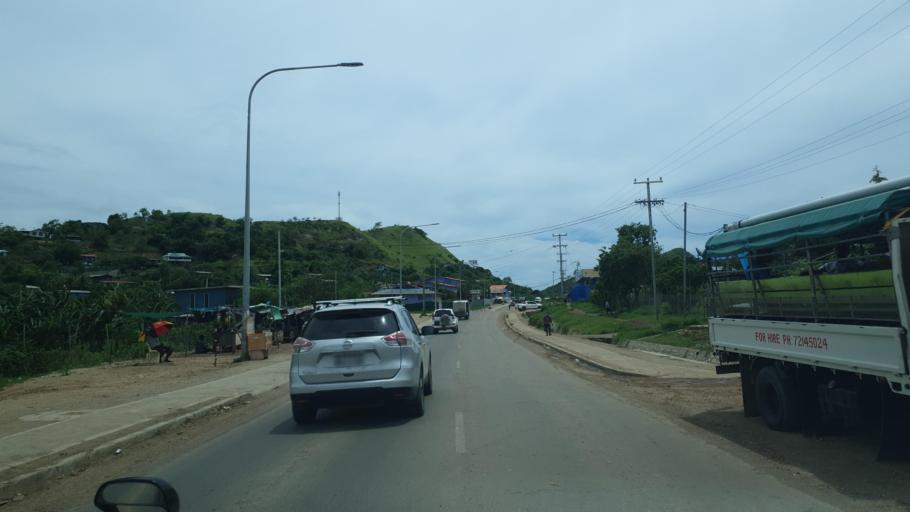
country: PG
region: National Capital
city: Port Moresby
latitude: -9.5179
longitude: 147.2405
